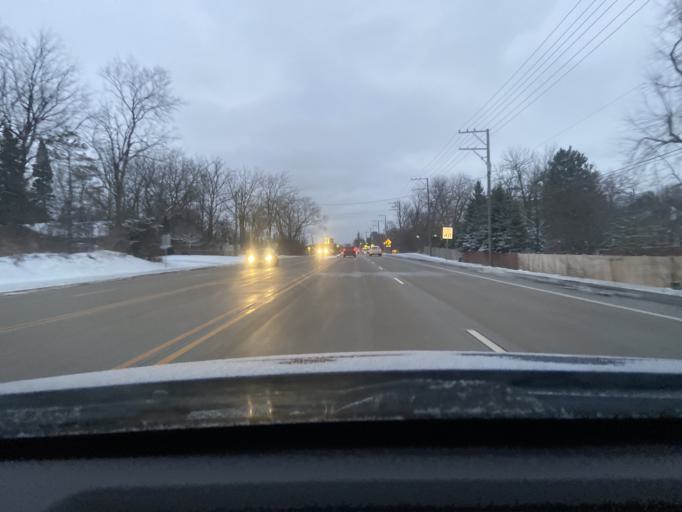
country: US
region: Illinois
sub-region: Lake County
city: Hainesville
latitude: 42.3570
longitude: -88.0561
